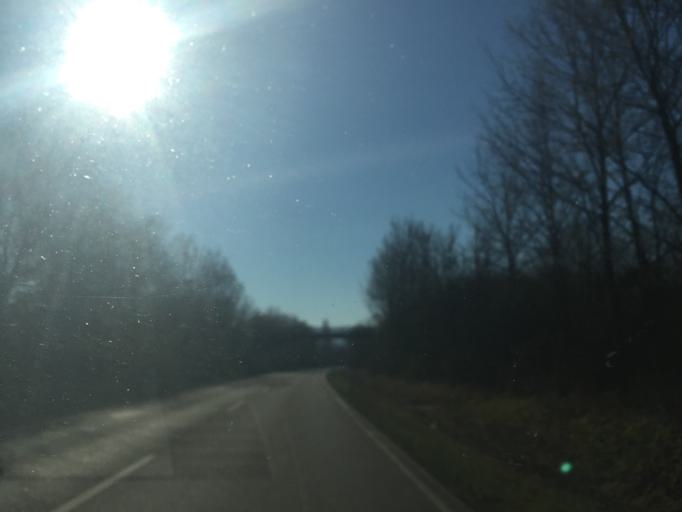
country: DE
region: Baden-Wuerttemberg
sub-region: Karlsruhe Region
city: Dossenheim
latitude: 49.4452
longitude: 8.6567
